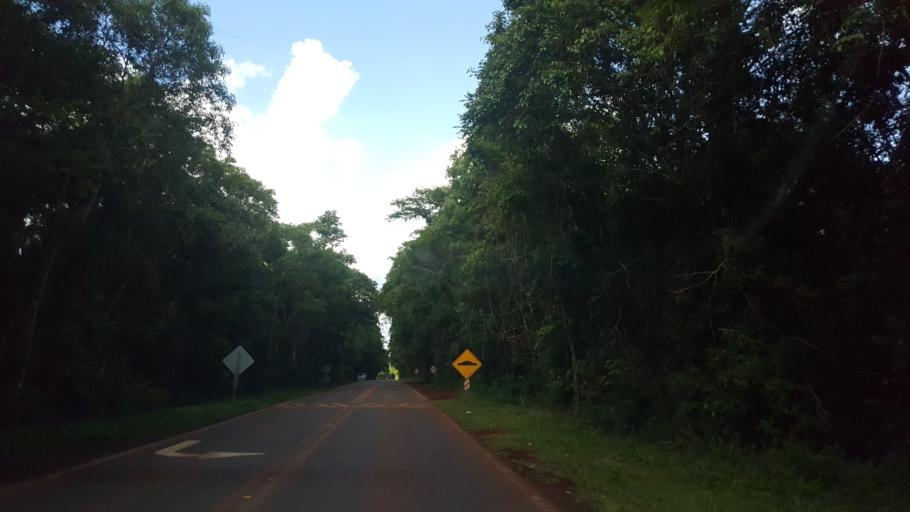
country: AR
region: Misiones
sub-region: Departamento de Iguazu
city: Puerto Iguazu
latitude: -25.7239
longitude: -54.4690
